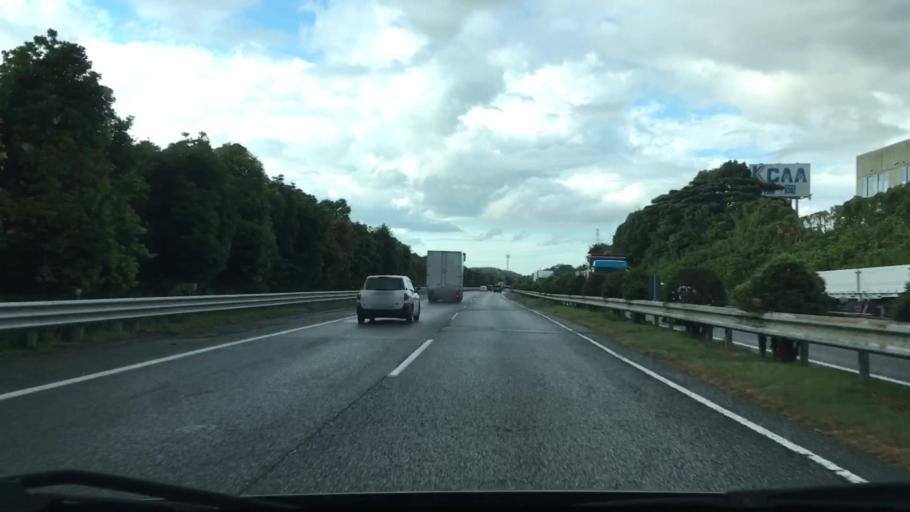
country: JP
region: Fukuoka
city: Koga
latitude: 33.6996
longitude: 130.4853
